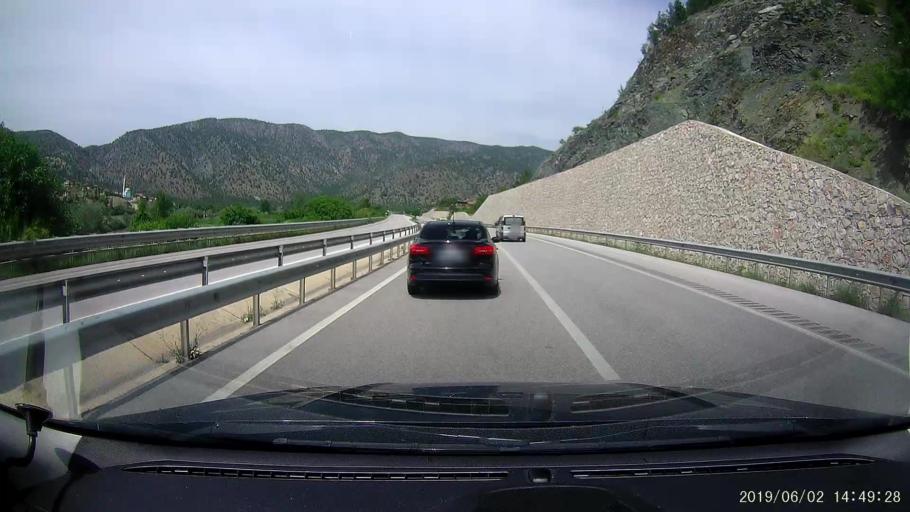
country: TR
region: Corum
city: Hacihamza
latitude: 41.0660
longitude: 34.5023
